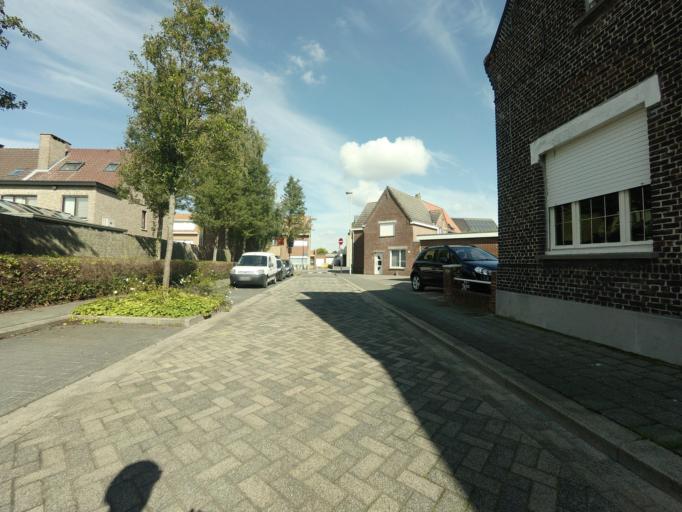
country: BE
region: Flanders
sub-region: Provincie Antwerpen
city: Boom
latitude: 51.0919
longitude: 4.3916
